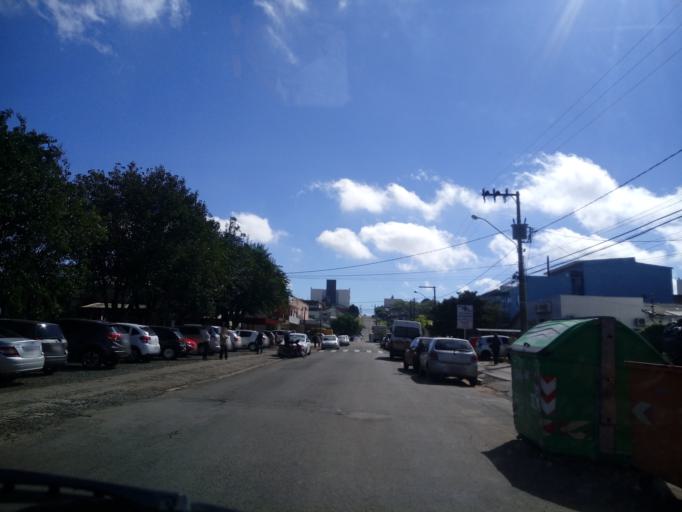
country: BR
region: Santa Catarina
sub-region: Chapeco
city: Chapeco
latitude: -27.1094
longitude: -52.6034
